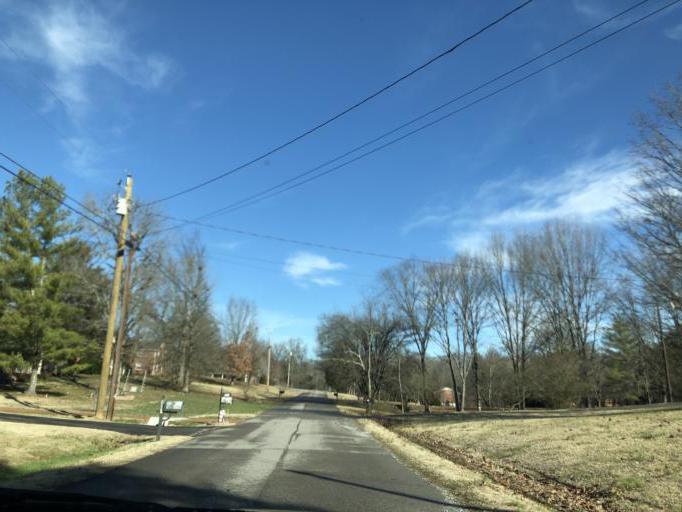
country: US
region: Tennessee
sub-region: Wilson County
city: Mount Juliet
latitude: 36.1810
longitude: -86.5251
